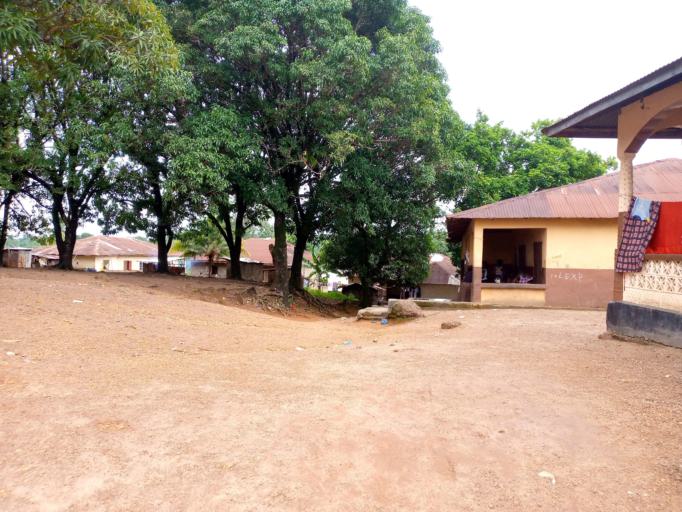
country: SL
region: Northern Province
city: Magburaka
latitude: 8.7242
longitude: -11.9501
